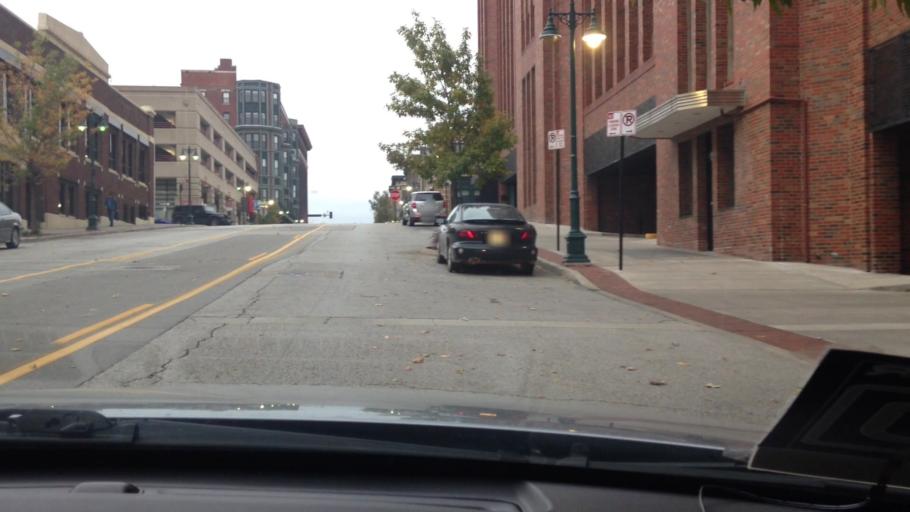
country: US
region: Missouri
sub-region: Jackson County
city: Kansas City
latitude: 39.1024
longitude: -94.5859
